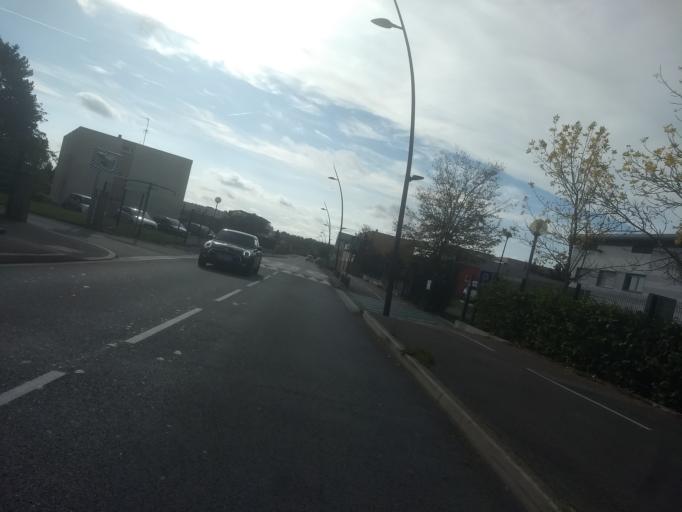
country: FR
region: Nord-Pas-de-Calais
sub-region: Departement du Pas-de-Calais
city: Dainville
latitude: 50.2913
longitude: 2.7354
